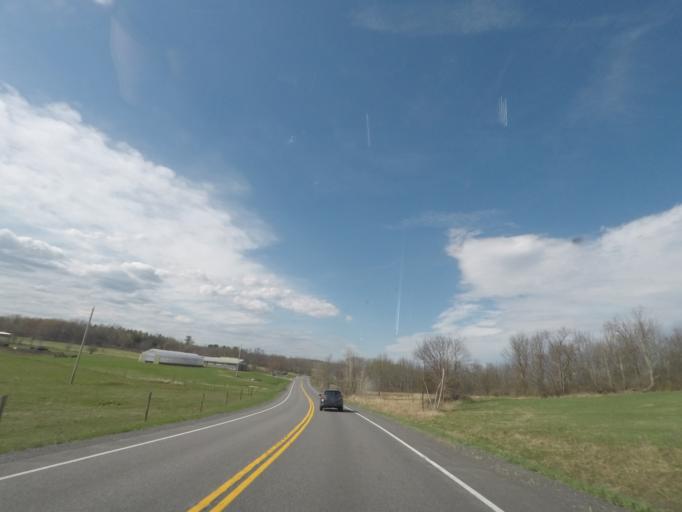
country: US
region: New York
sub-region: Greene County
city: Cairo
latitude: 42.4728
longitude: -74.0004
